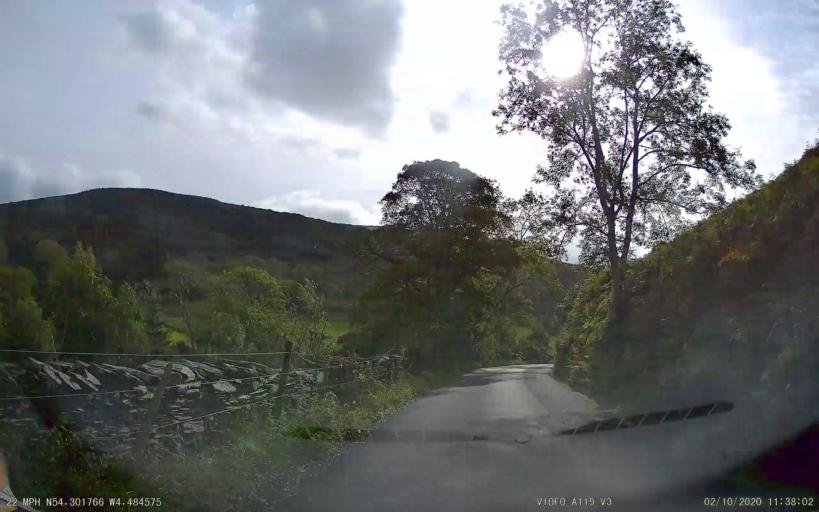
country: IM
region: Ramsey
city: Ramsey
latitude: 54.3018
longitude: -4.4846
